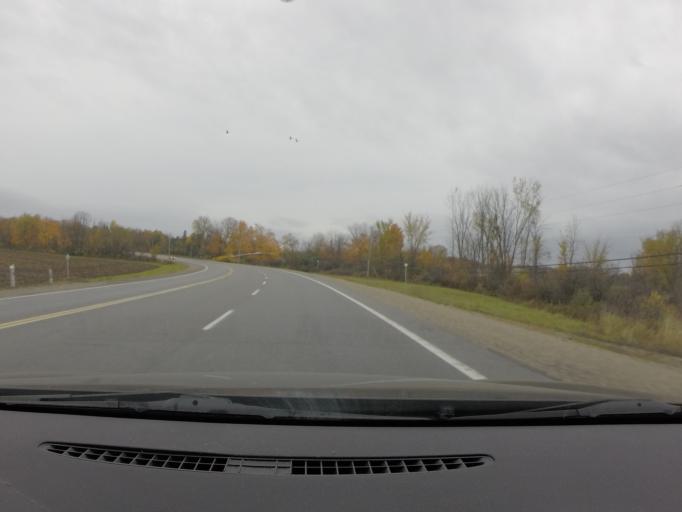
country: CA
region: Ontario
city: Carleton Place
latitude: 45.1333
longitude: -76.1965
